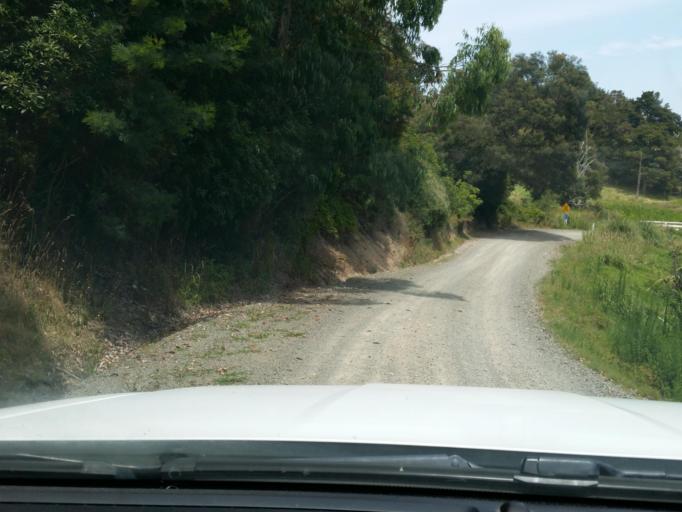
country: NZ
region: Northland
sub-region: Whangarei
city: Ruakaka
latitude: -36.0366
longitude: 174.2632
